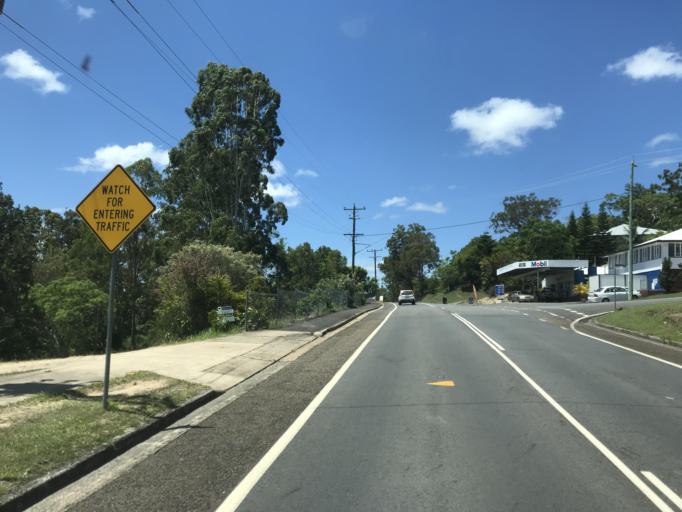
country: AU
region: Queensland
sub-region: Tablelands
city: Atherton
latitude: -17.3870
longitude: 145.3870
